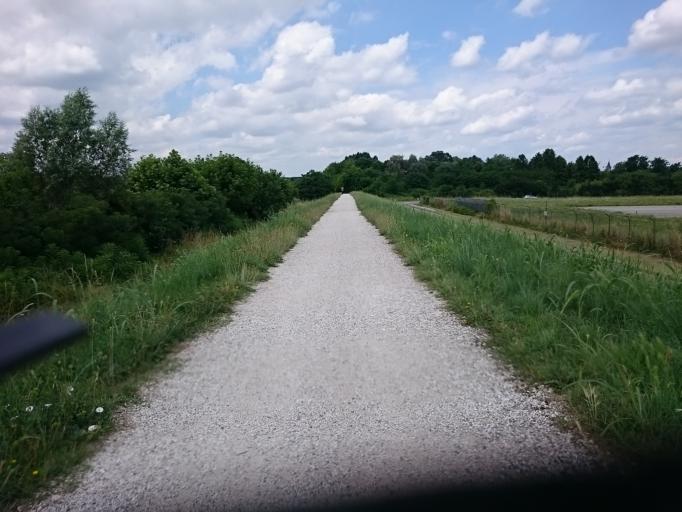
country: IT
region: Veneto
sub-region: Provincia di Padova
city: Mandriola-Sant'Agostino
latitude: 45.3907
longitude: 11.8429
